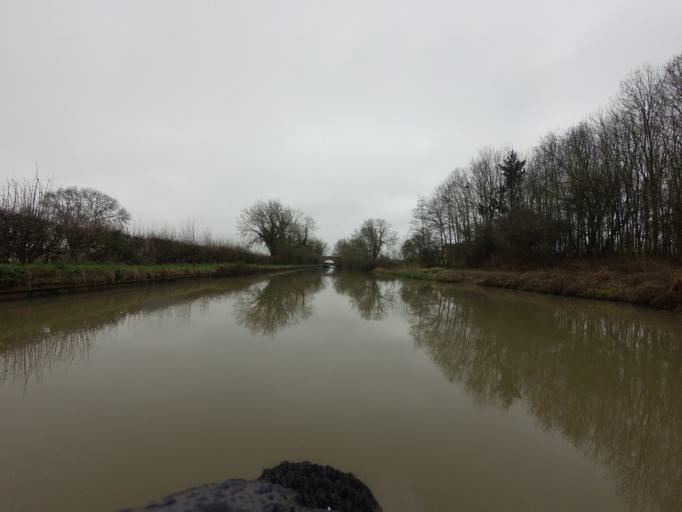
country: GB
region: England
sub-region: Milton Keynes
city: Castlethorpe
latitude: 52.0948
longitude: -0.8620
